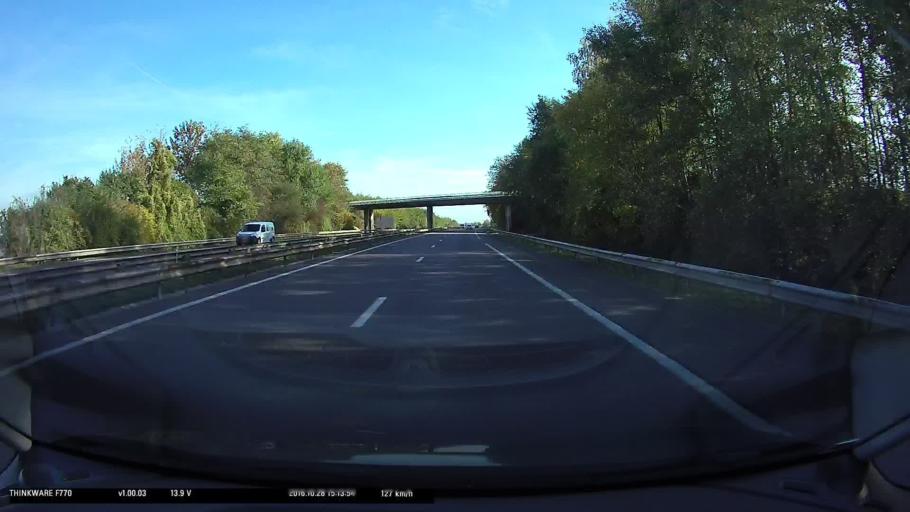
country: FR
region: Alsace
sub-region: Departement du Bas-Rhin
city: Mommenheim
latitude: 48.7607
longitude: 7.6654
